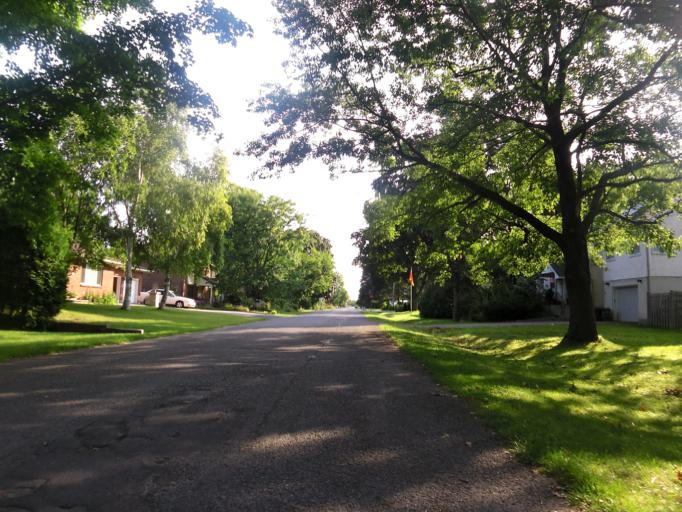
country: CA
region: Ontario
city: Ottawa
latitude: 45.3568
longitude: -75.7445
